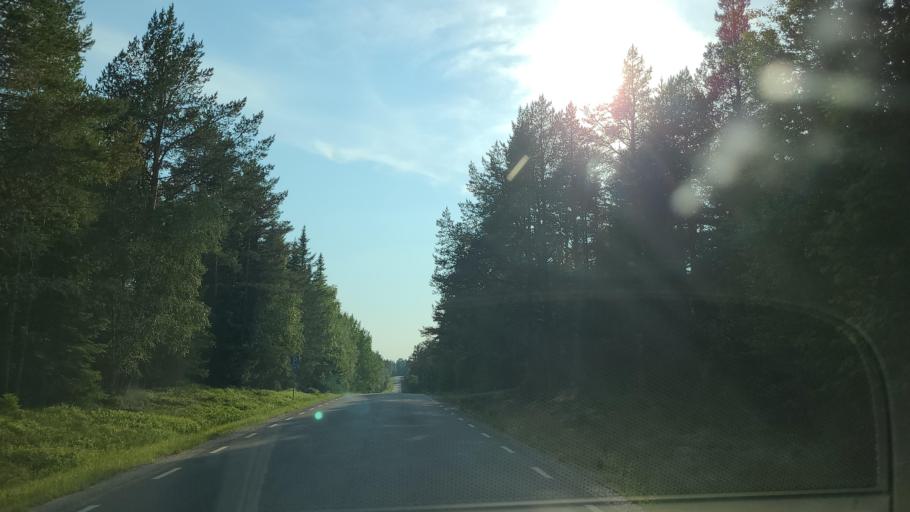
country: SE
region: Vaesterbotten
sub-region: Skelleftea Kommun
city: Burea
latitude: 64.4520
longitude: 21.5722
